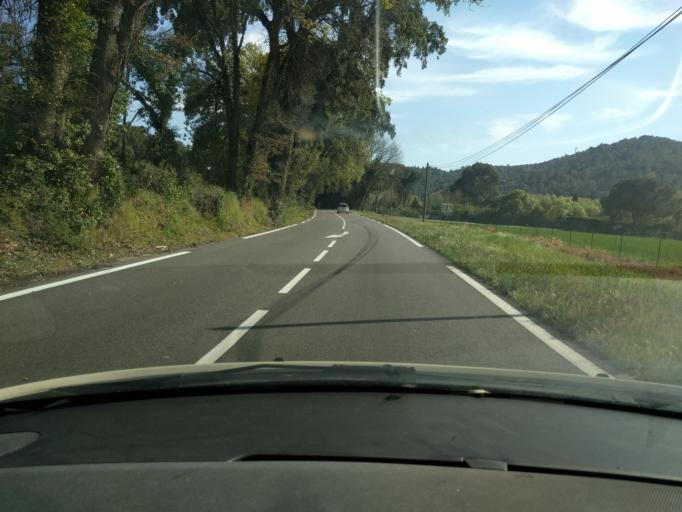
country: FR
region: Provence-Alpes-Cote d'Azur
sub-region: Departement du Var
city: La Crau
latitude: 43.1695
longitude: 6.1184
